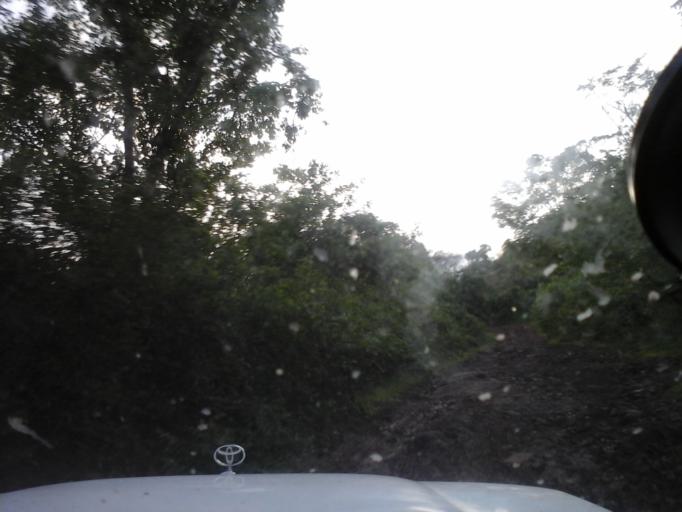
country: CO
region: Cesar
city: Agustin Codazzi
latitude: 10.1734
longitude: -73.1530
